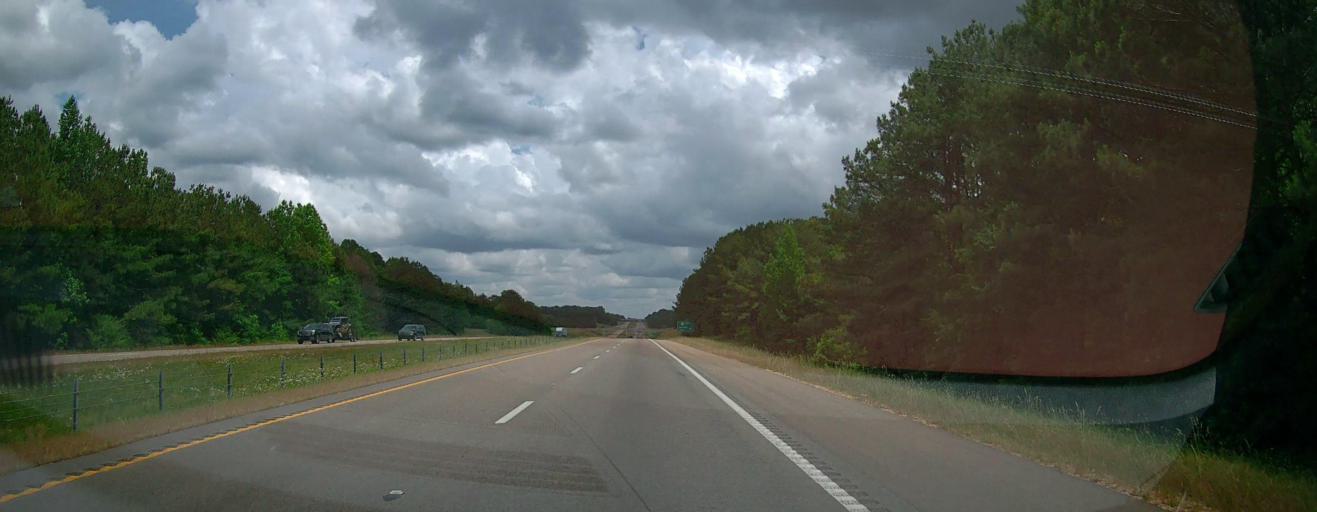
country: US
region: Mississippi
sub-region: Itawamba County
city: Fulton
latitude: 34.2395
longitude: -88.3488
